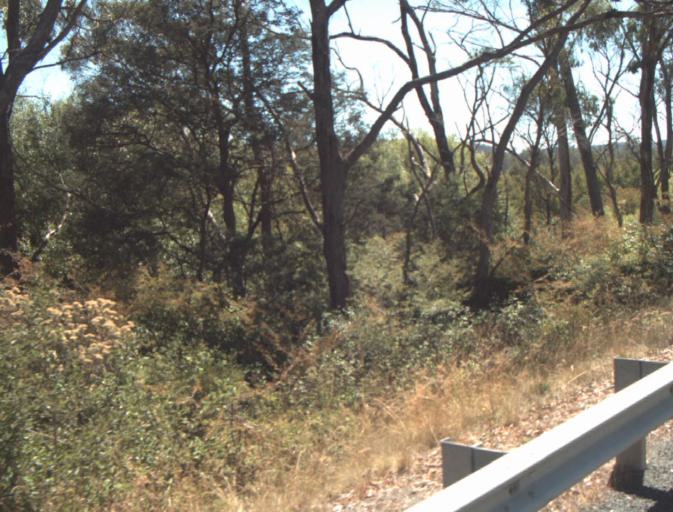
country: AU
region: Tasmania
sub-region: Launceston
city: Newstead
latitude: -41.3729
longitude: 147.3147
